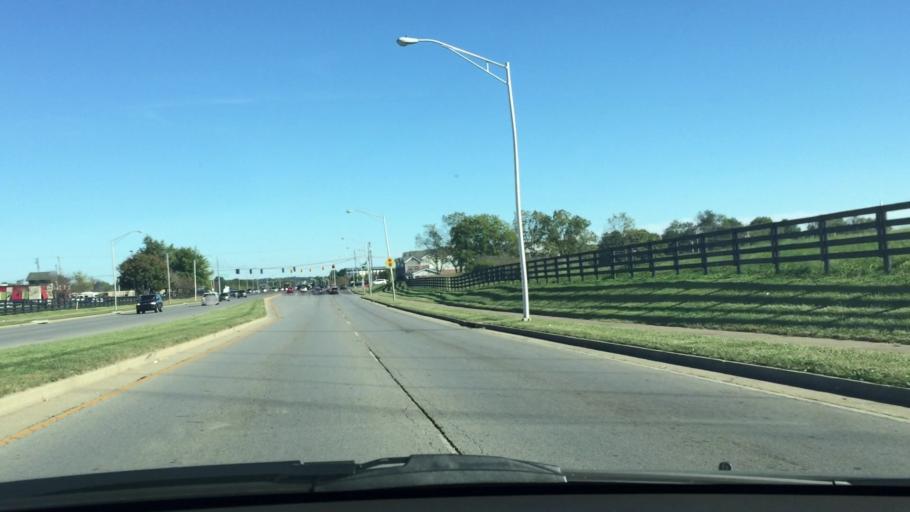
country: US
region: Kentucky
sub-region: Fayette County
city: Monticello
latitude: 37.9773
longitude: -84.5330
